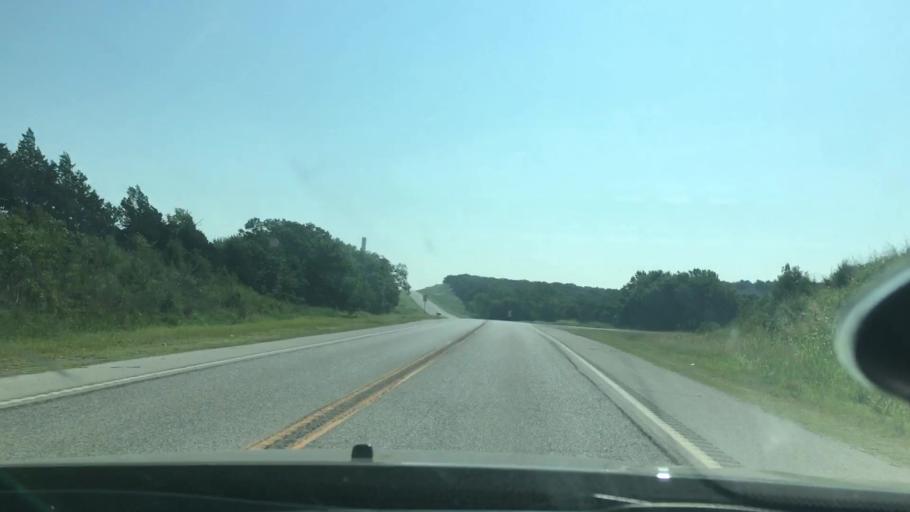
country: US
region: Oklahoma
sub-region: Carter County
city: Dickson
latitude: 34.0957
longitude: -96.9711
